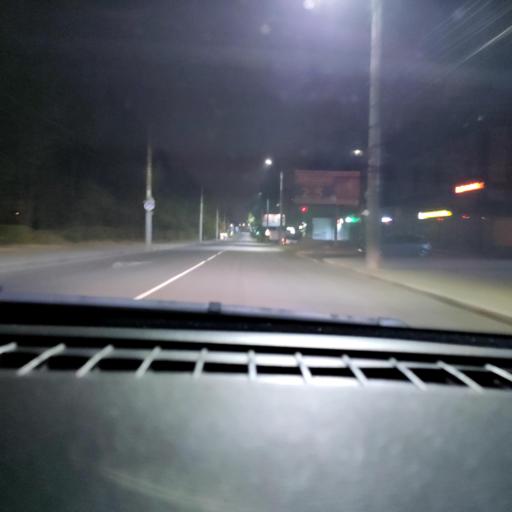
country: RU
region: Voronezj
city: Pridonskoy
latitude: 51.6516
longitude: 39.1249
